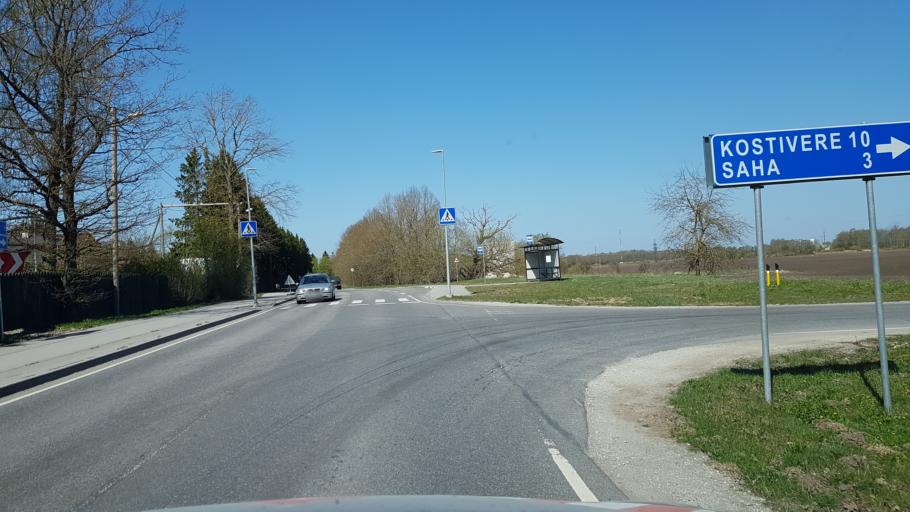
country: EE
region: Harju
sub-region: Joelaehtme vald
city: Loo
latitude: 59.4156
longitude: 24.9451
